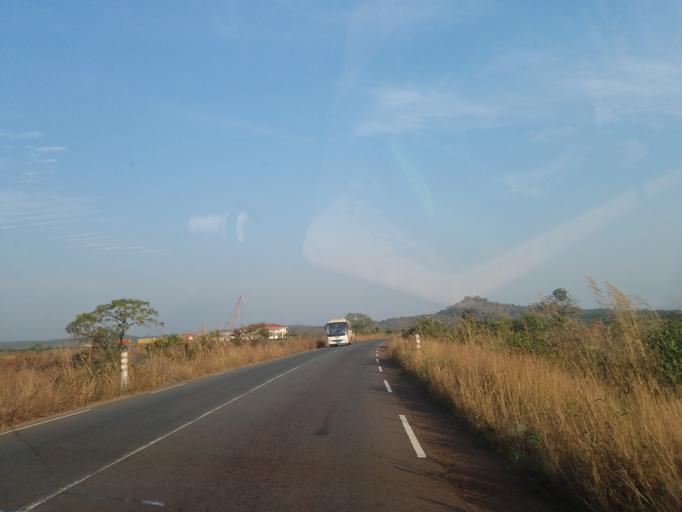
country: GN
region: Boke
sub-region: Boffa
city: Boffa
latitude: 10.3516
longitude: -14.2534
